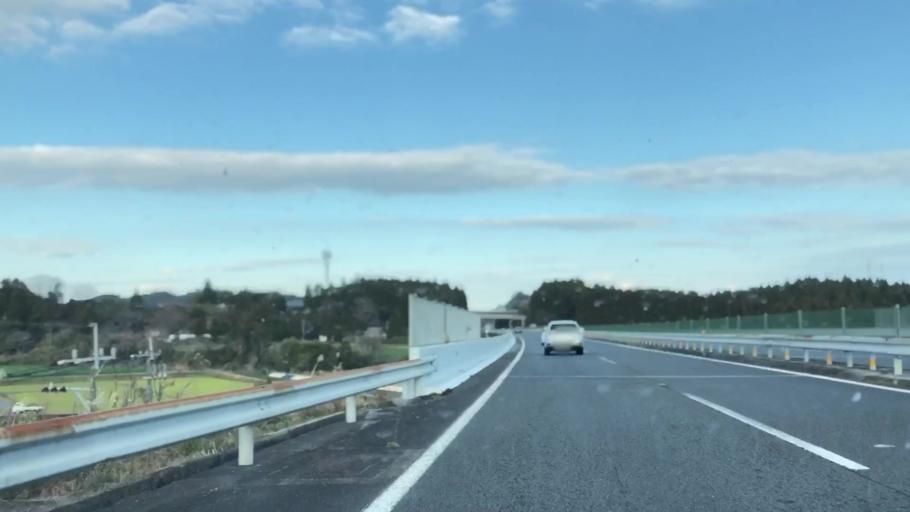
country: JP
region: Miyazaki
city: Miyazaki-shi
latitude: 31.8554
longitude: 131.3734
